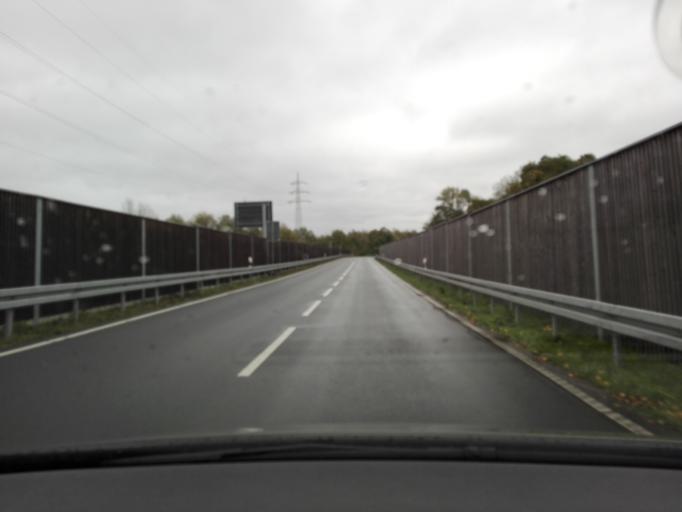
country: DE
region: North Rhine-Westphalia
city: Selm
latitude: 51.6827
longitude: 7.4715
